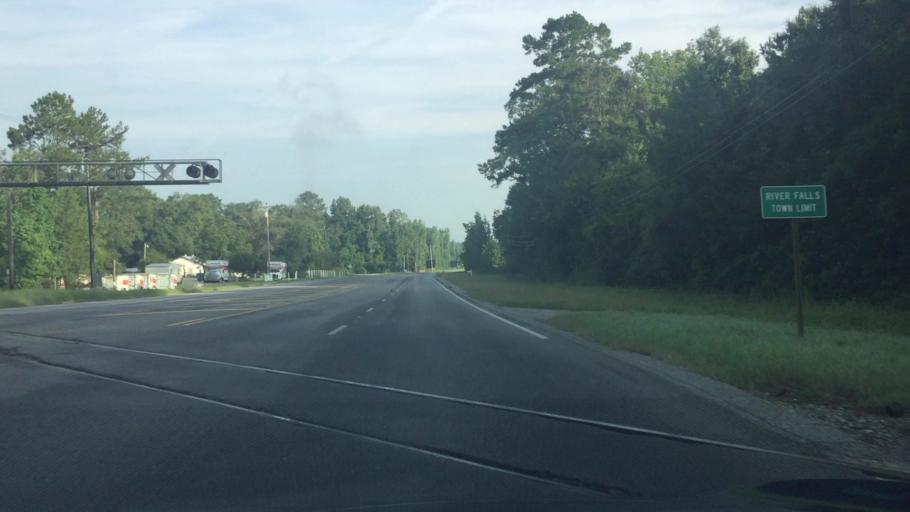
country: US
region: Alabama
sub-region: Covington County
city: Andalusia
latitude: 31.3363
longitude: -86.5204
